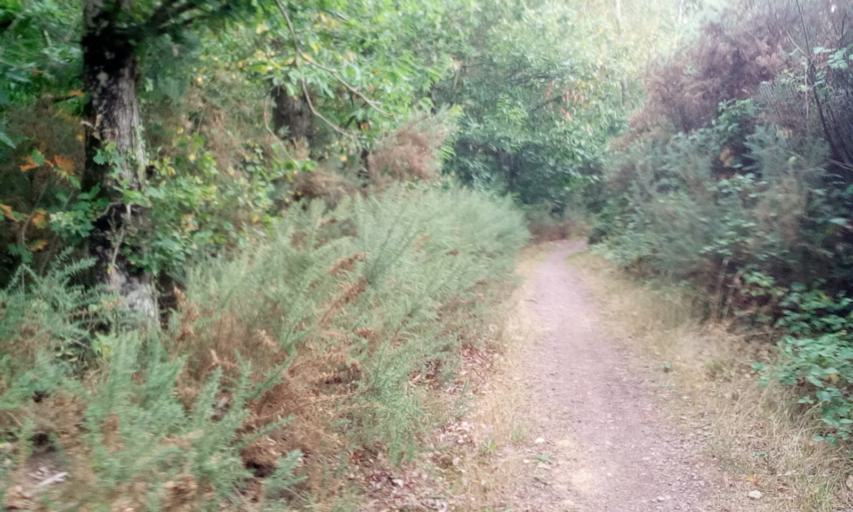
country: FR
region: Lower Normandy
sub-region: Departement du Calvados
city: Mouen
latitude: 49.1377
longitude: -0.4817
